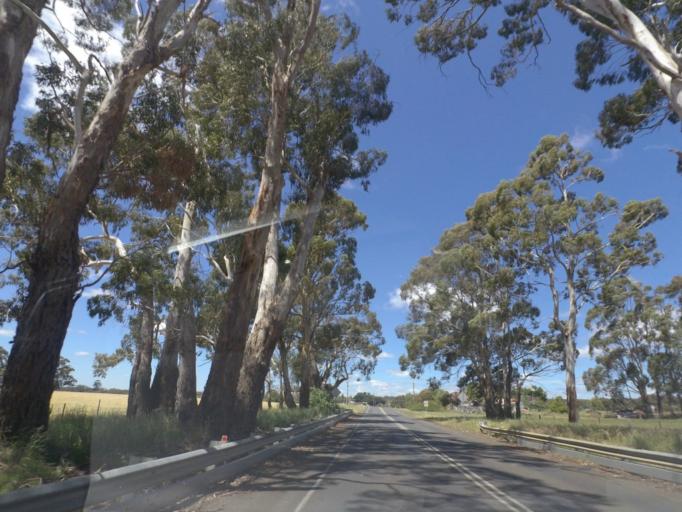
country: AU
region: Victoria
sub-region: Mount Alexander
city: Castlemaine
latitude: -37.3308
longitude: 144.1786
